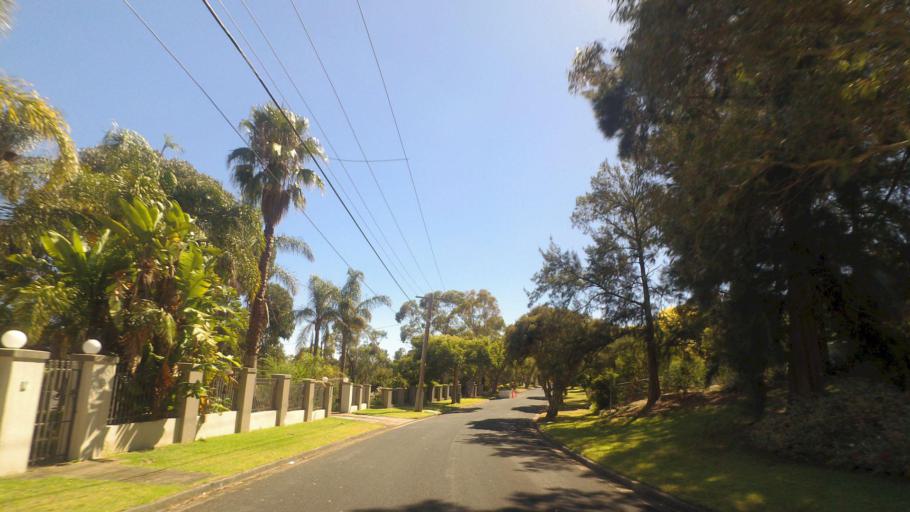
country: AU
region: Victoria
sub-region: Manningham
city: Donvale
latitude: -37.7963
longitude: 145.1918
